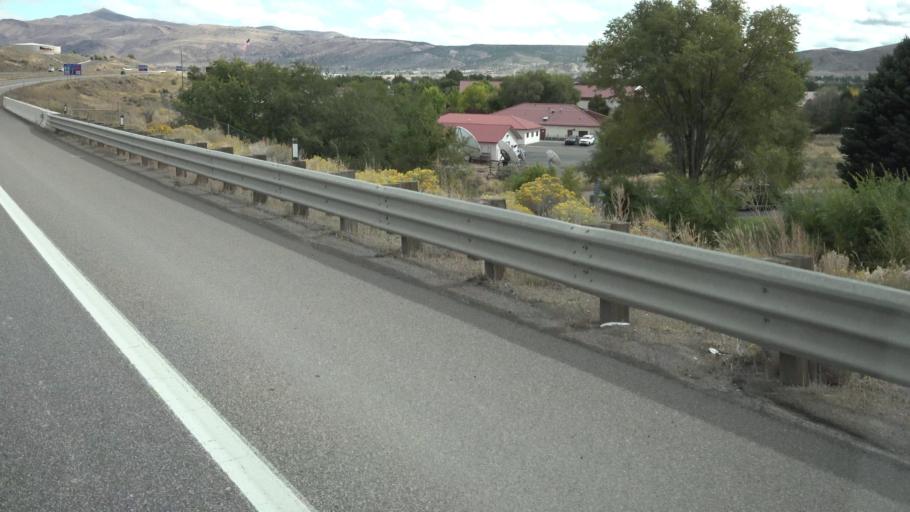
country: US
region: Nevada
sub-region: Elko County
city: Elko
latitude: 40.8437
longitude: -115.7714
